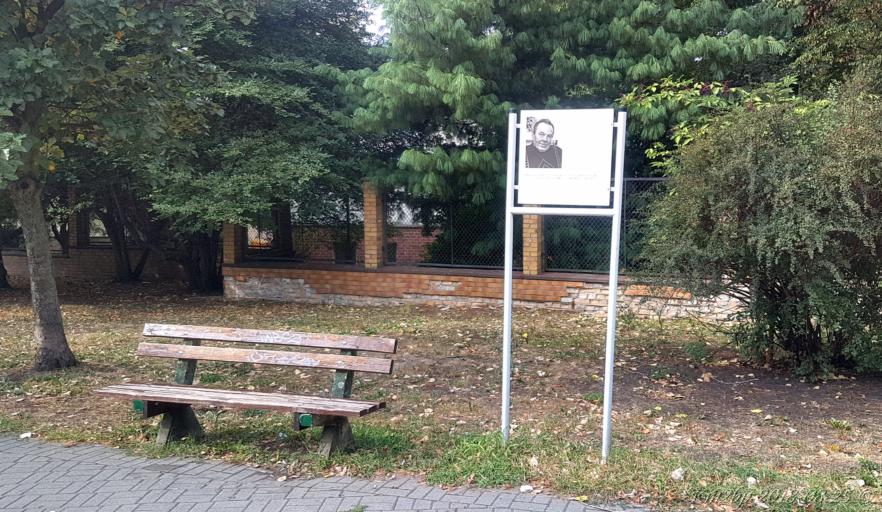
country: PL
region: Lubusz
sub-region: Zielona Gora
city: Zielona Gora
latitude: 51.9397
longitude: 15.5194
